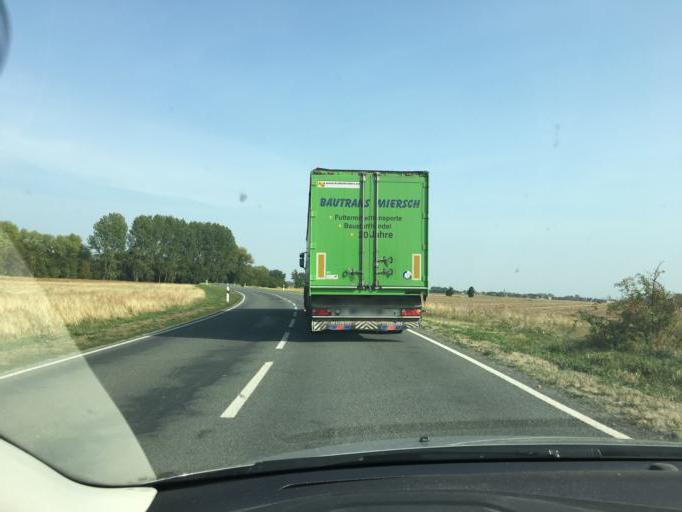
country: DE
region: Saxony-Anhalt
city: Plotzky
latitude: 52.0035
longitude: 11.8075
